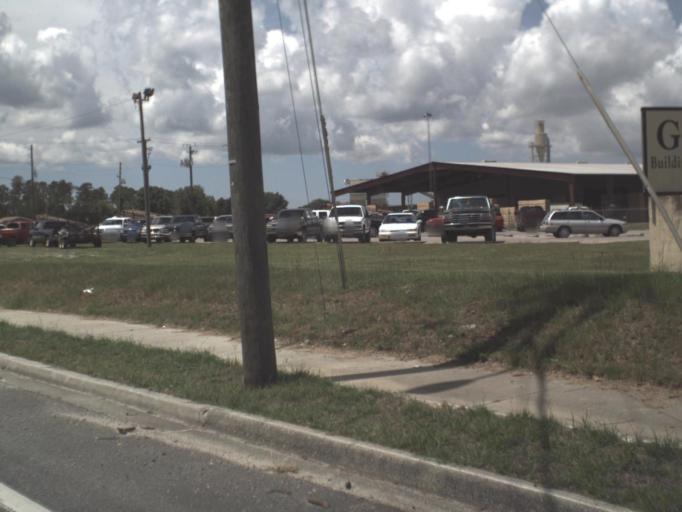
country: US
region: Florida
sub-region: Taylor County
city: Perry
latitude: 30.1065
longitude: -83.5893
